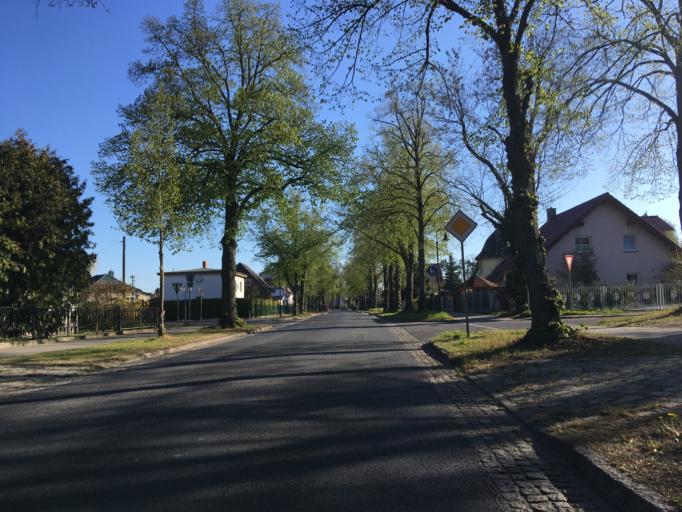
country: DE
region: Berlin
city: Buch
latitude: 52.6718
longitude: 13.5345
